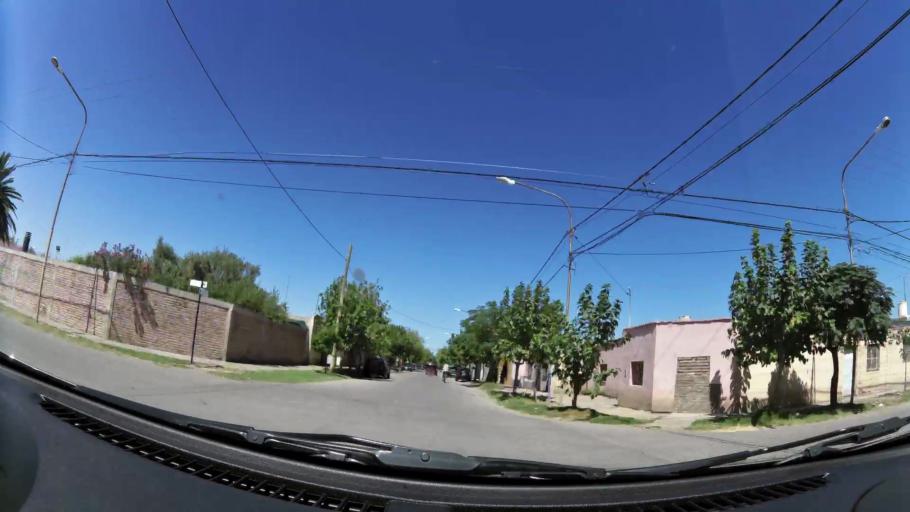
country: AR
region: San Juan
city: San Juan
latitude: -31.5180
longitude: -68.5205
